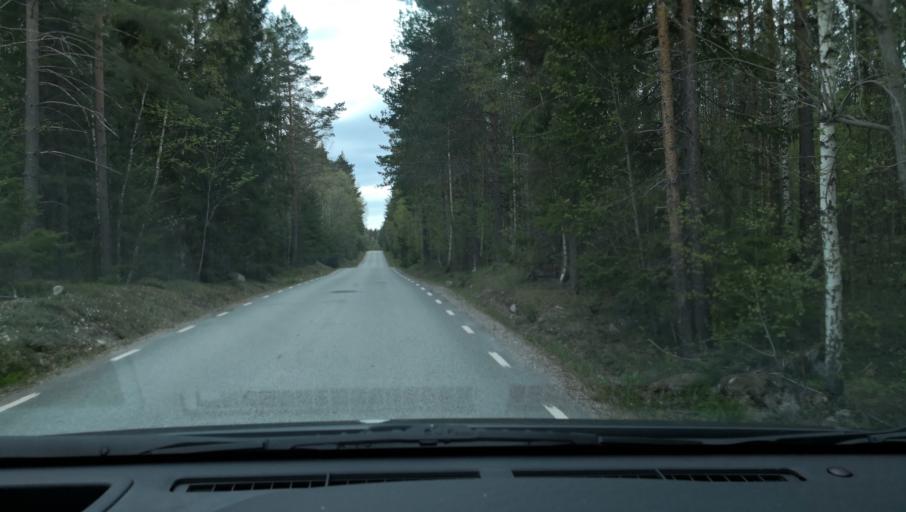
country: SE
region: Vaestmanland
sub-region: Norbergs Kommun
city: Norberg
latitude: 60.0906
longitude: 15.8920
